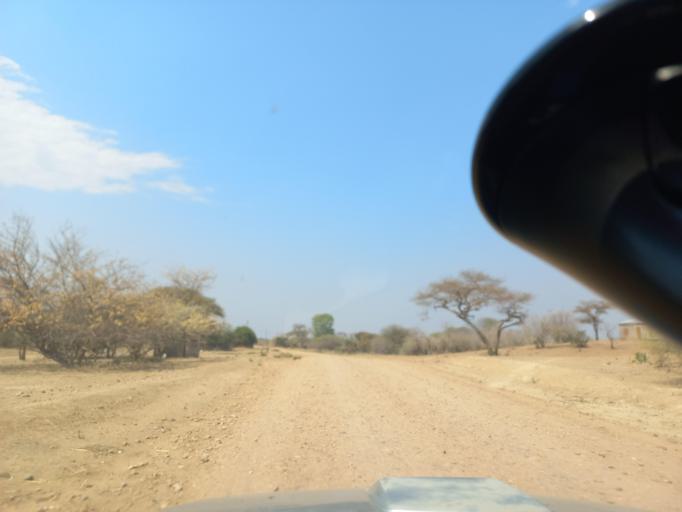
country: ZW
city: Chirundu
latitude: -15.9405
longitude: 28.8515
